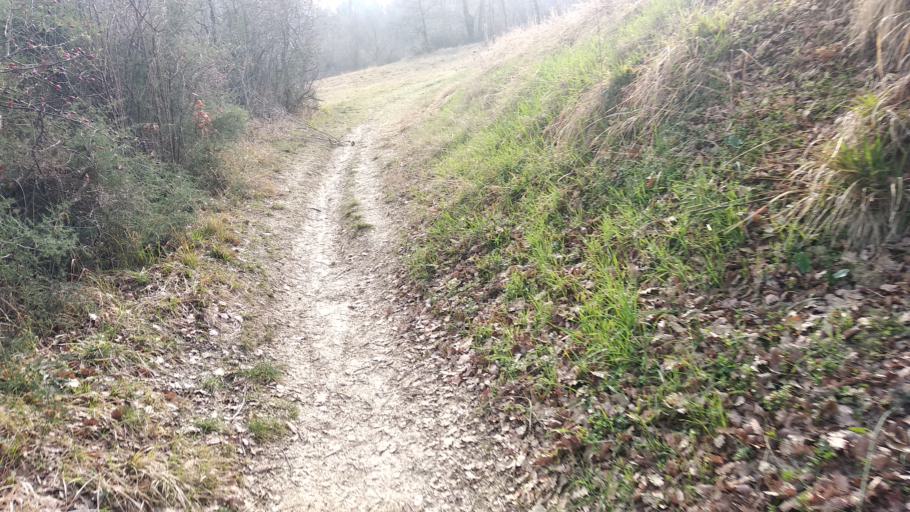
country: IT
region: Emilia-Romagna
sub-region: Provincia di Bologna
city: Ponticella
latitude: 44.4439
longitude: 11.3745
